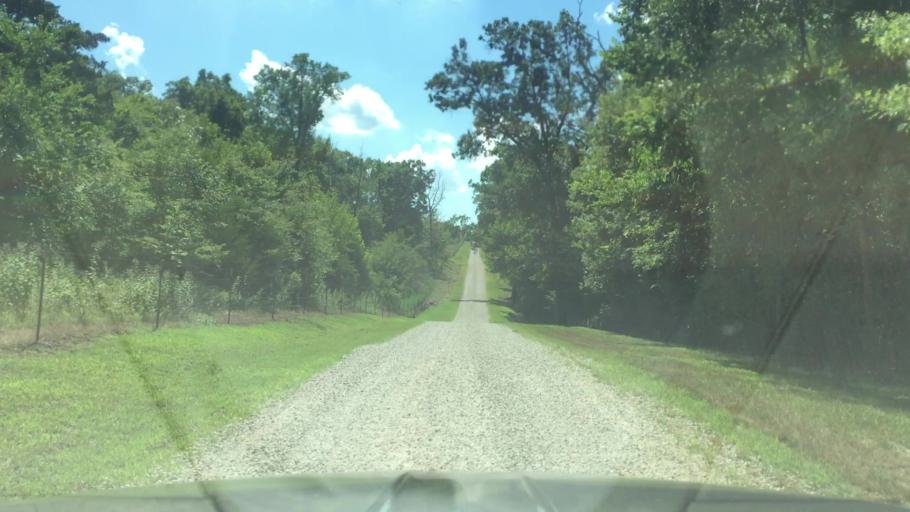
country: US
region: Missouri
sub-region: Miller County
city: Tuscumbia
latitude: 38.1311
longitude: -92.4521
